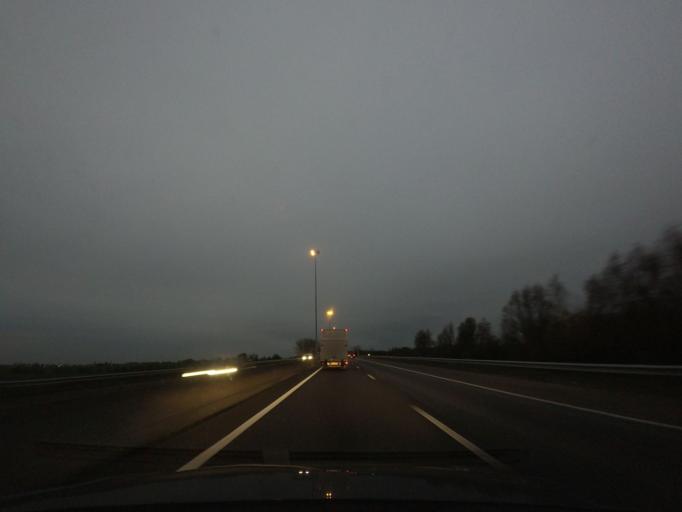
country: NL
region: Utrecht
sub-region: Gemeente Lopik
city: Lopik
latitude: 51.9380
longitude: 5.0023
